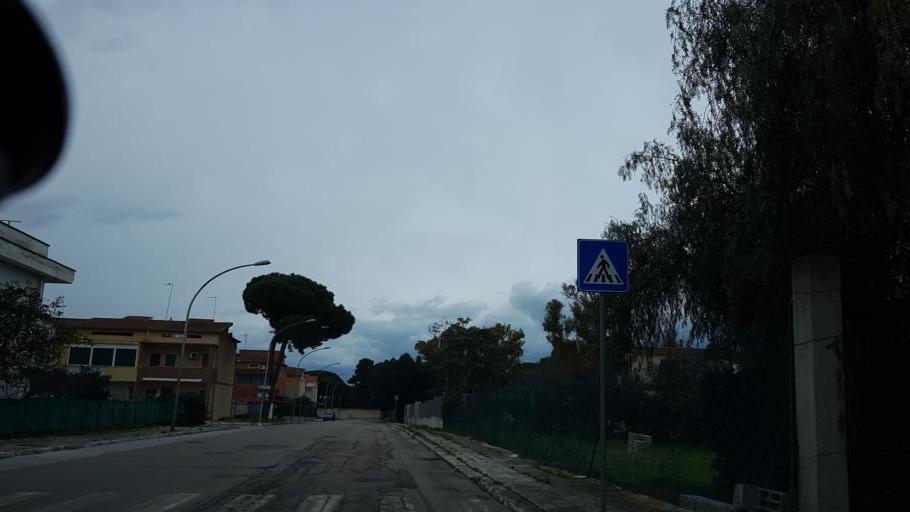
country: IT
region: Apulia
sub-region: Provincia di Brindisi
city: La Rosa
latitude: 40.6080
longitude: 17.9533
